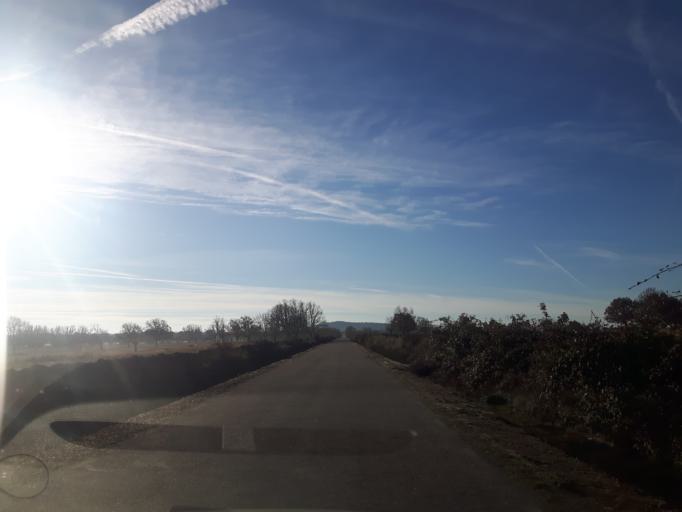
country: ES
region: Castille and Leon
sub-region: Provincia de Salamanca
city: Olmedo de Camaces
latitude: 40.9312
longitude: -6.6189
